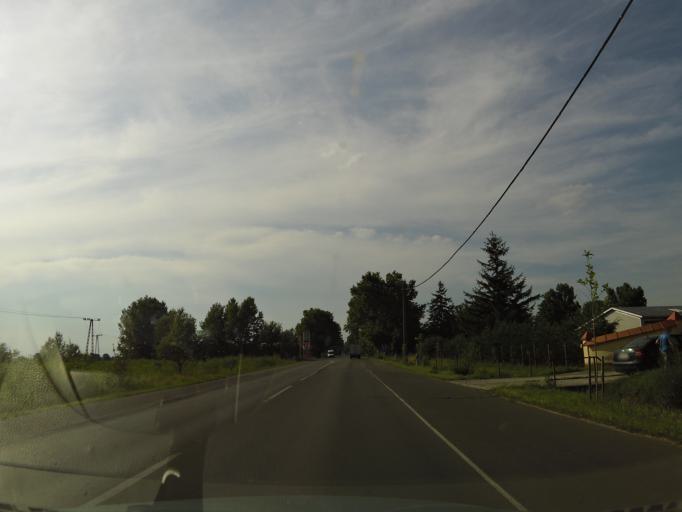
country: HU
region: Csongrad
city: Balastya
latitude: 46.4133
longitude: 20.0190
